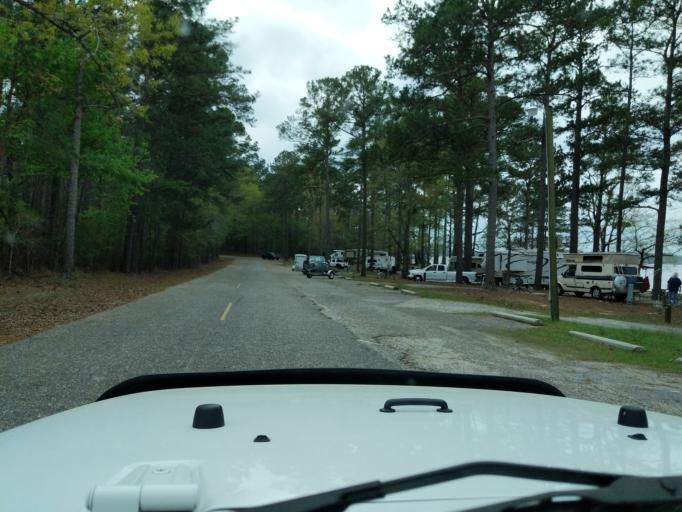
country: US
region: Georgia
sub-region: Clay County
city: Fort Gaines
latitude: 31.6738
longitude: -85.0652
